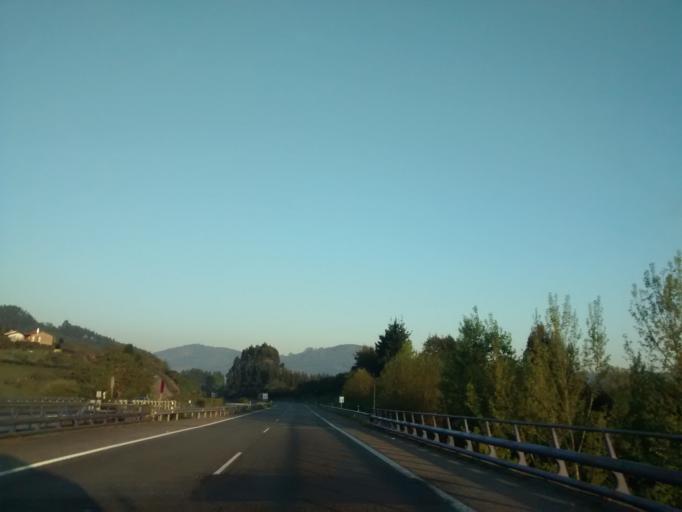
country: ES
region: Asturias
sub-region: Province of Asturias
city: Villaviciosa
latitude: 43.5007
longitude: -5.3900
